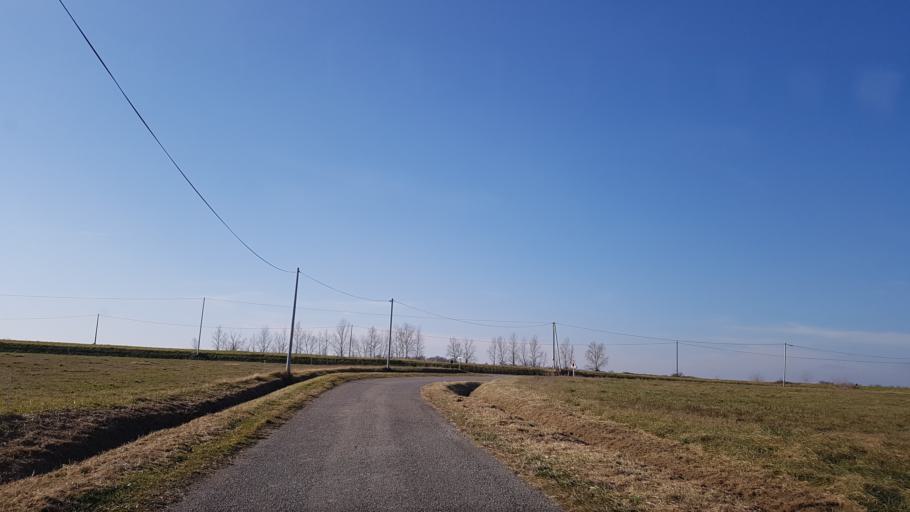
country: FR
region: Midi-Pyrenees
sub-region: Departement de l'Ariege
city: La Tour-du-Crieu
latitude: 43.1487
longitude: 1.7029
